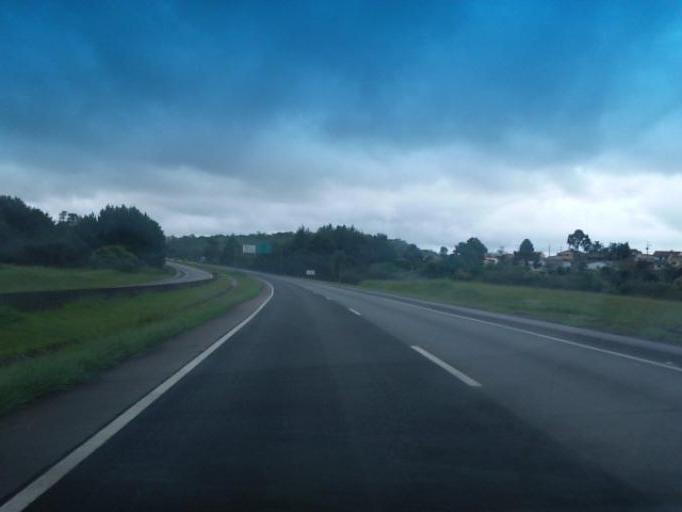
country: BR
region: Parana
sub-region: Piraquara
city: Piraquara
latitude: -25.4560
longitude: -49.0877
